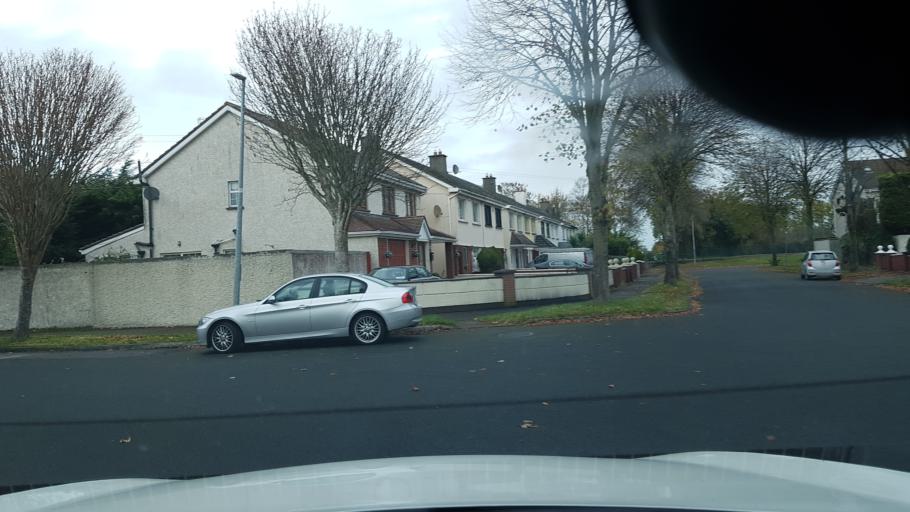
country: IE
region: Leinster
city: Hartstown
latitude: 53.3933
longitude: -6.4152
